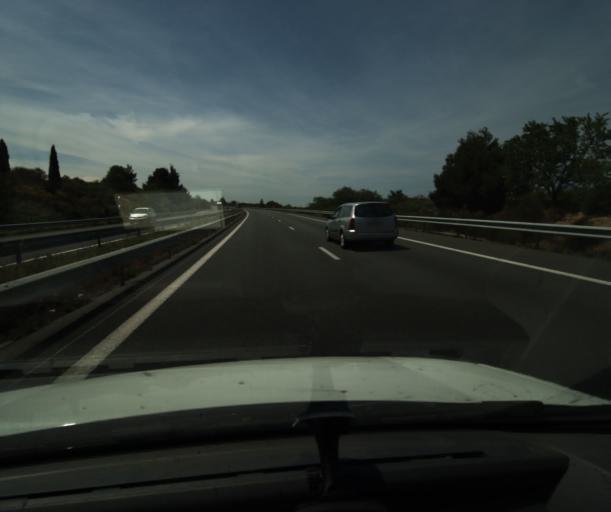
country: FR
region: Languedoc-Roussillon
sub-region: Departement de l'Aude
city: Capendu
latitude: 43.1820
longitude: 2.5236
